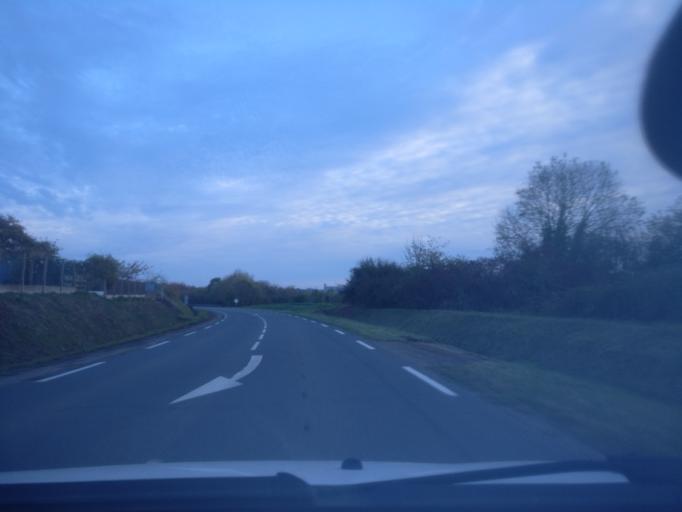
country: FR
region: Brittany
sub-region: Departement d'Ille-et-Vilaine
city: Cancale
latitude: 48.6602
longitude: -1.8678
